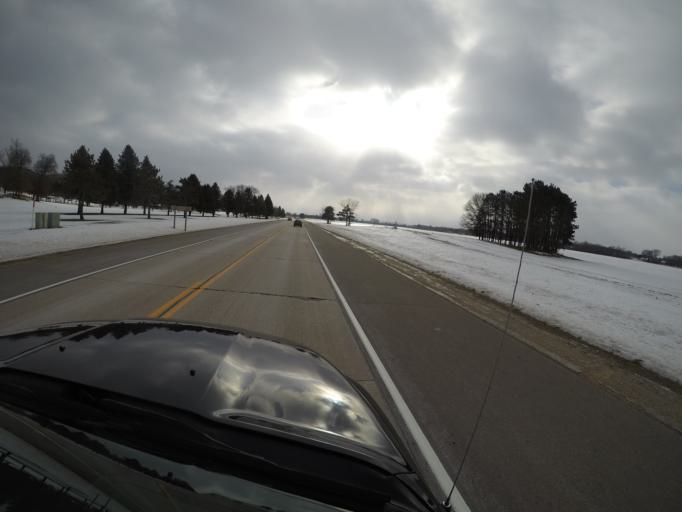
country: US
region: Wisconsin
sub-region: Trempealeau County
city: Galesville
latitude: 44.0333
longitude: -91.2907
